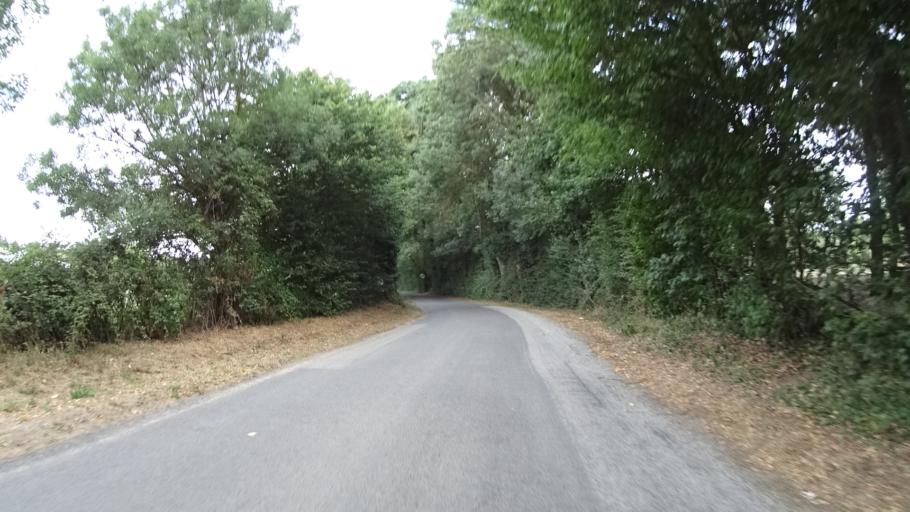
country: FR
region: Pays de la Loire
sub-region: Departement de la Loire-Atlantique
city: Oudon
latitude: 47.3473
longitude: -1.2765
